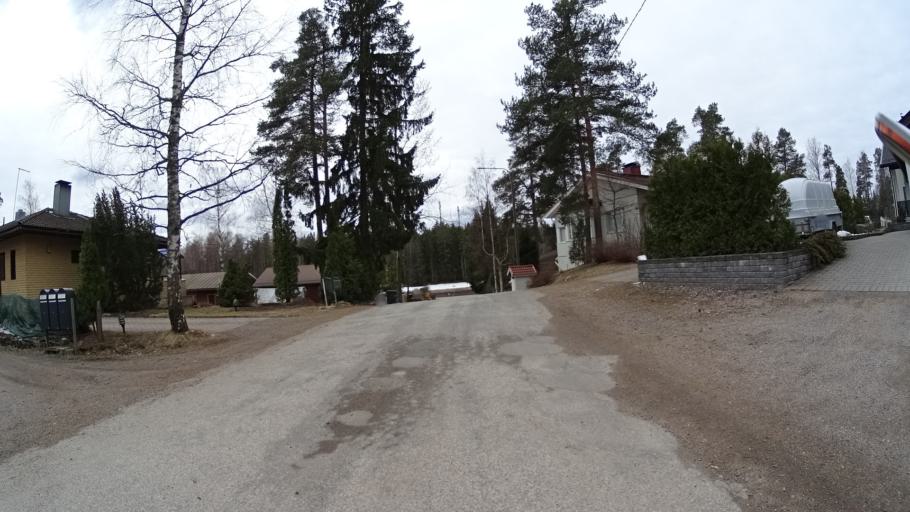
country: FI
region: Uusimaa
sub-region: Helsinki
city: Teekkarikylae
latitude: 60.2783
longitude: 24.9045
